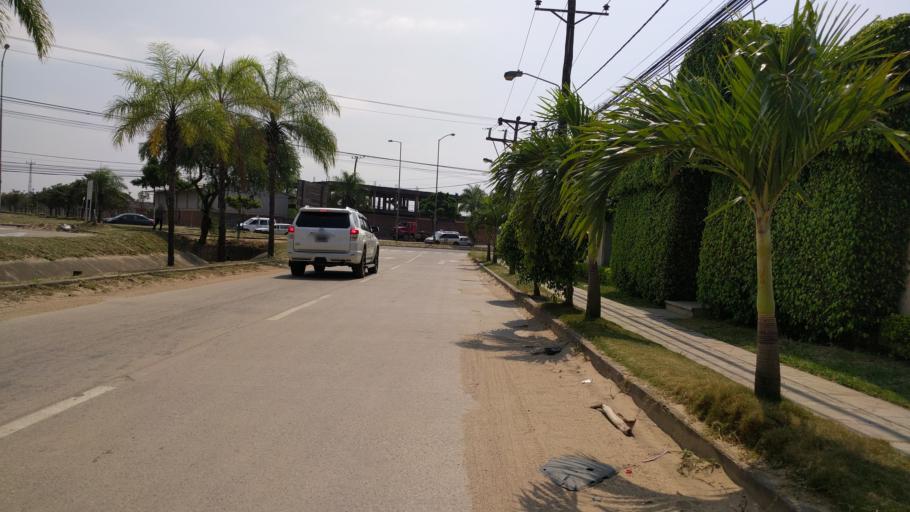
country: BO
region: Santa Cruz
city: Santa Cruz de la Sierra
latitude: -17.8183
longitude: -63.2147
